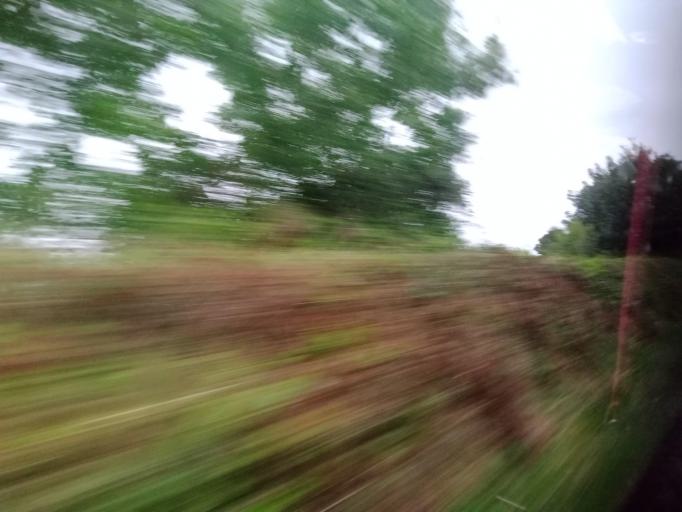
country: IE
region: Munster
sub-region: Waterford
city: Dungarvan
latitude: 52.0501
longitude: -7.6411
